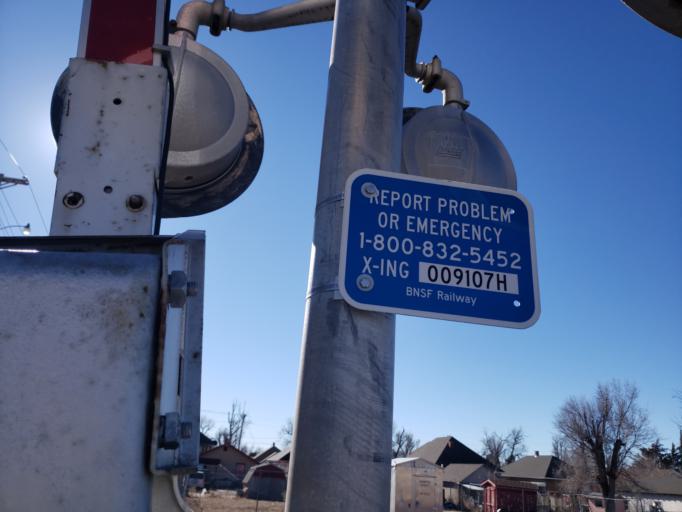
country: US
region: Kansas
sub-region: Ford County
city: Dodge City
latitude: 37.7529
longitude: -100.0294
